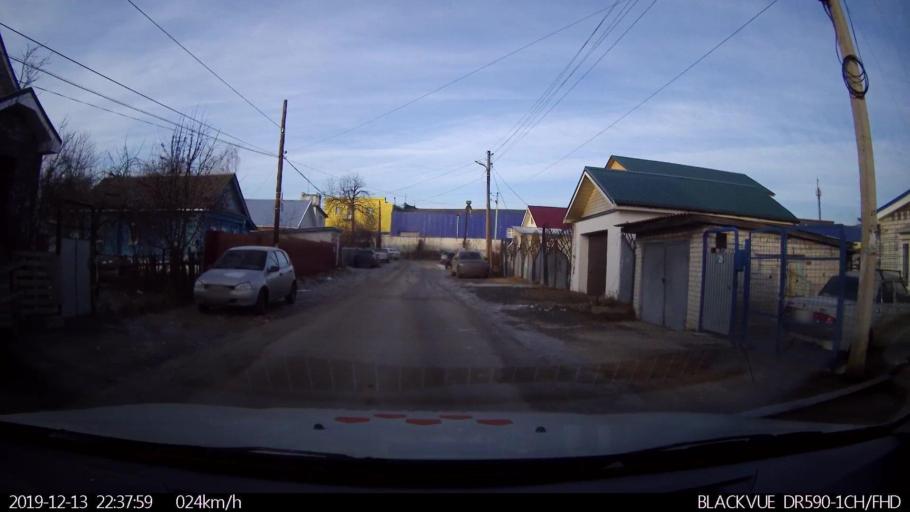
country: RU
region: Nizjnij Novgorod
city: Kstovo
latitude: 56.1752
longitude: 44.1665
